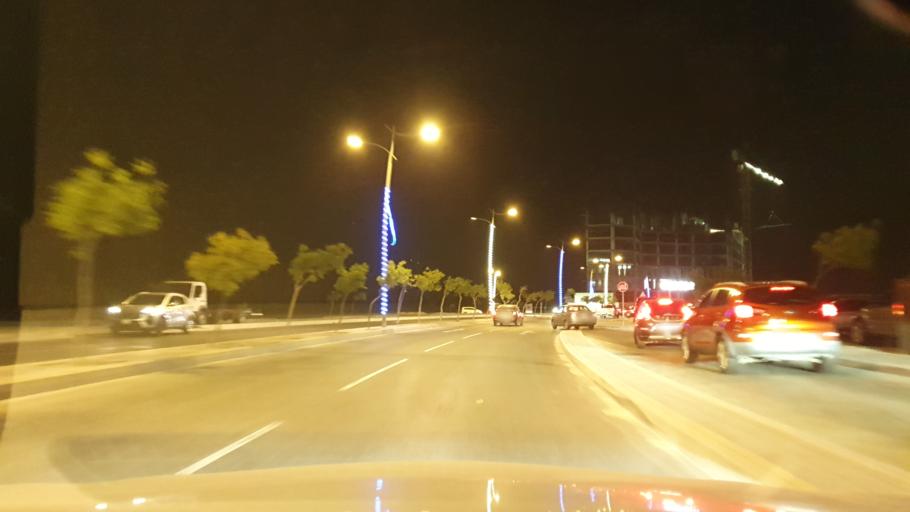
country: BH
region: Manama
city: Jidd Hafs
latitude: 26.2422
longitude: 50.5524
